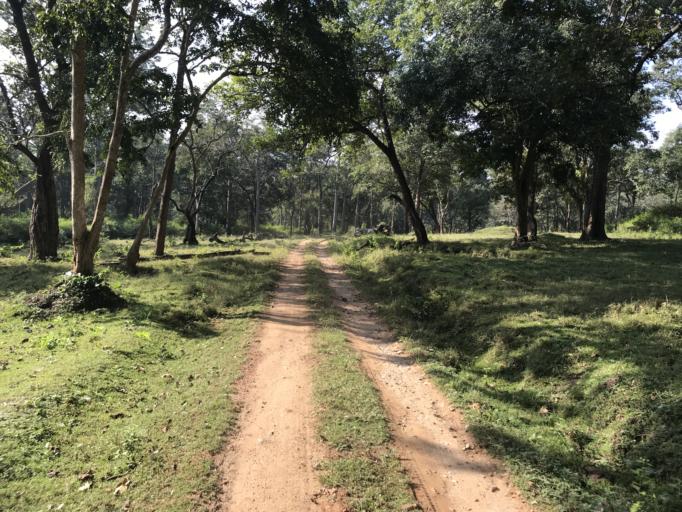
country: IN
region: Karnataka
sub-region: Mysore
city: Heggadadevankote
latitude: 11.9469
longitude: 76.2187
